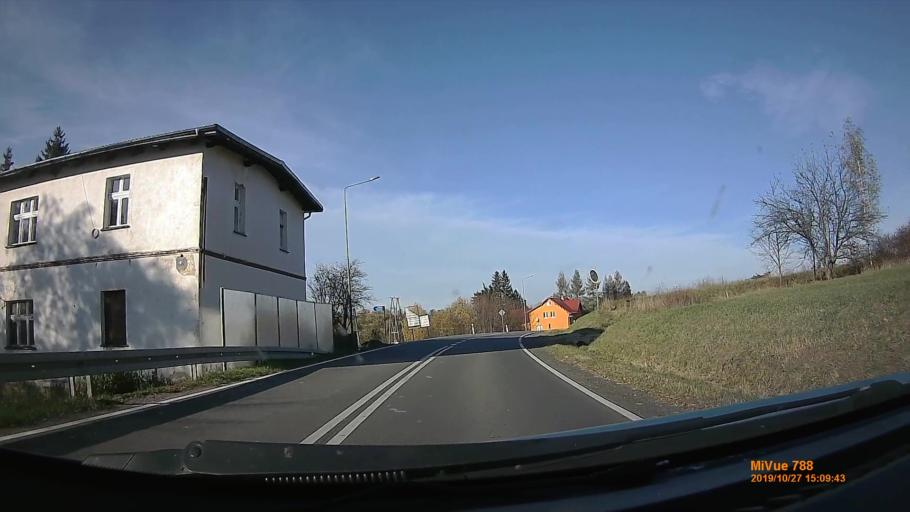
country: PL
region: Lower Silesian Voivodeship
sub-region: Powiat klodzki
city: Miedzylesie
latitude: 50.1821
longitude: 16.6682
